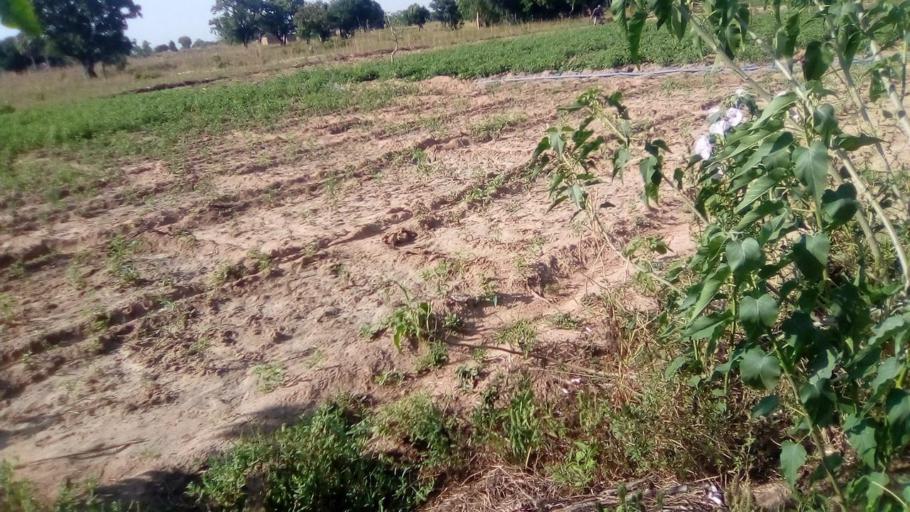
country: TG
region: Savanes
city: Dapaong
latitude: 11.0546
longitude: 0.1241
